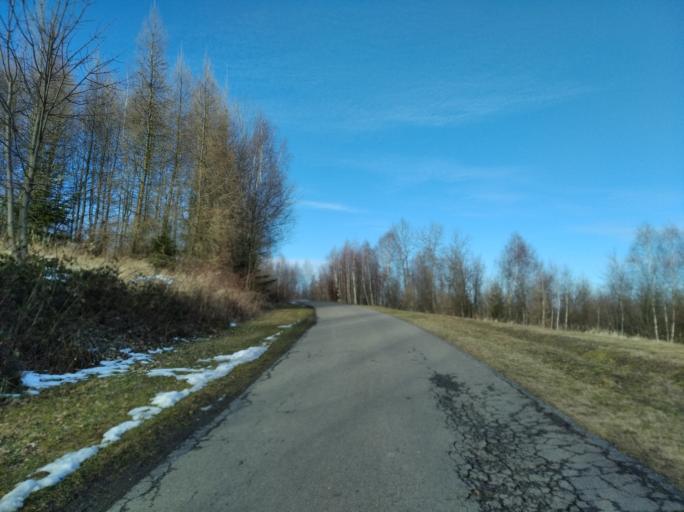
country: PL
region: Subcarpathian Voivodeship
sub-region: Powiat strzyzowski
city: Gwoznica Gorna
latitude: 49.8186
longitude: 21.9902
